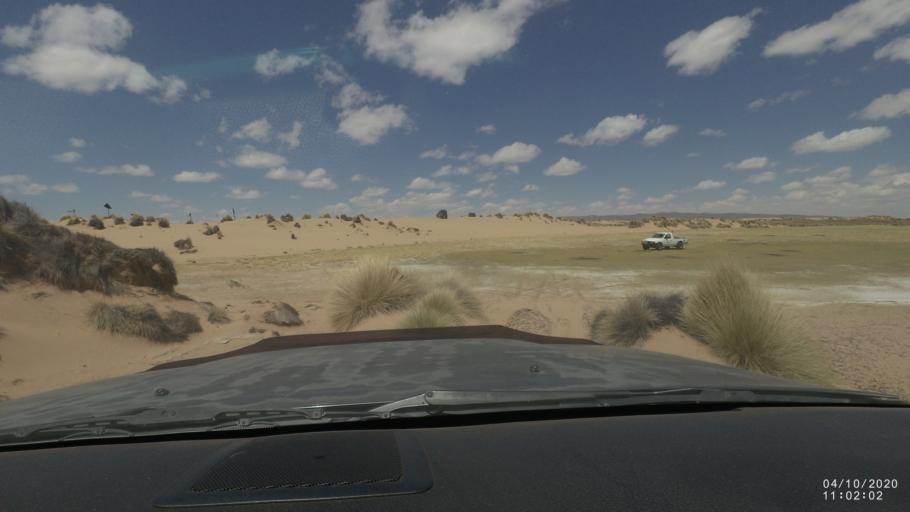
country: BO
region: Oruro
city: Poopo
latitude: -18.7009
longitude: -67.4673
